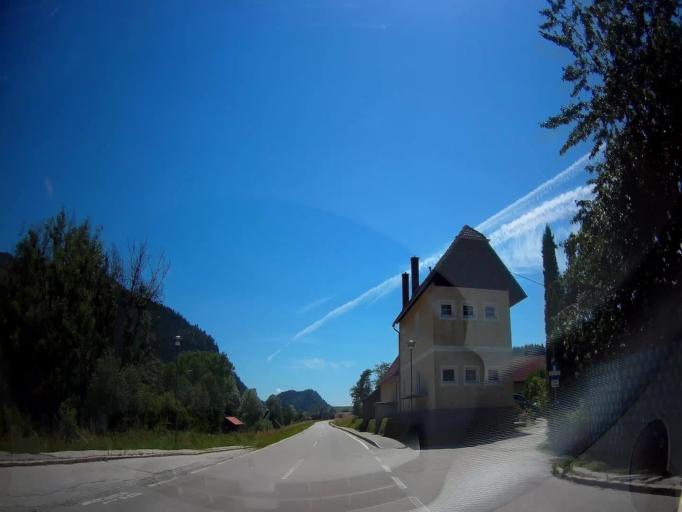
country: AT
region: Carinthia
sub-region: Politischer Bezirk Sankt Veit an der Glan
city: Micheldorf
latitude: 46.9086
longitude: 14.4340
